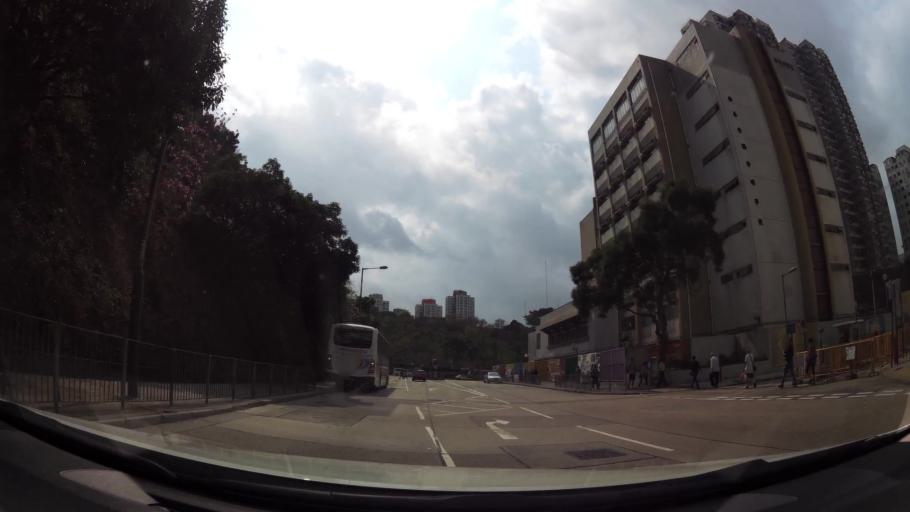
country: HK
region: Kowloon City
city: Kowloon
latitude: 22.3207
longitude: 114.2230
